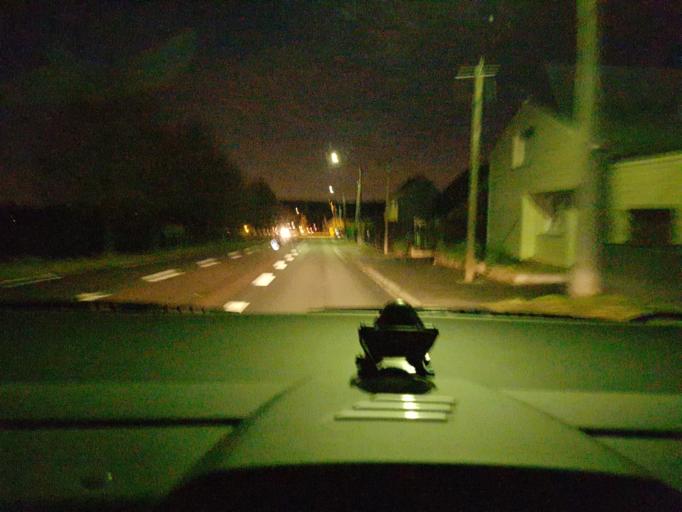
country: FR
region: Nord-Pas-de-Calais
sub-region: Departement du Pas-de-Calais
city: Souchez
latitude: 50.3831
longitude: 2.7437
